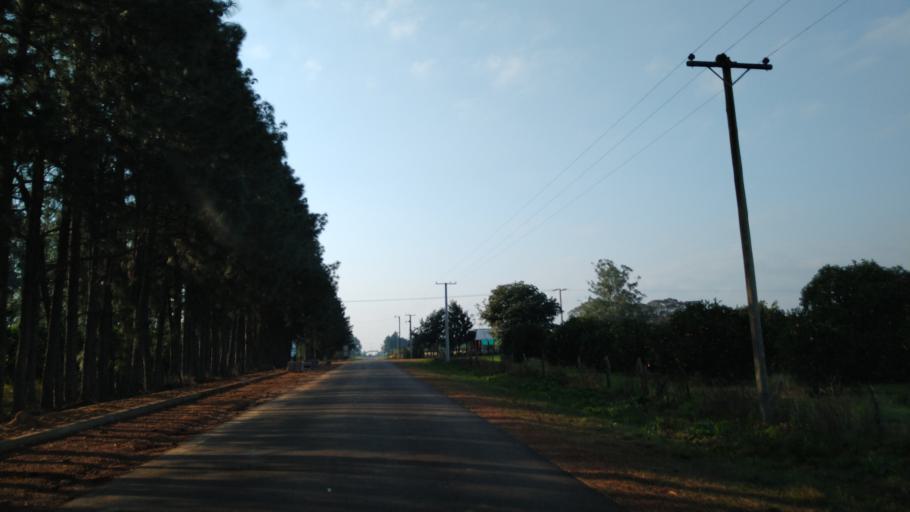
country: AR
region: Entre Rios
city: Santa Ana
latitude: -30.9054
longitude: -57.9253
